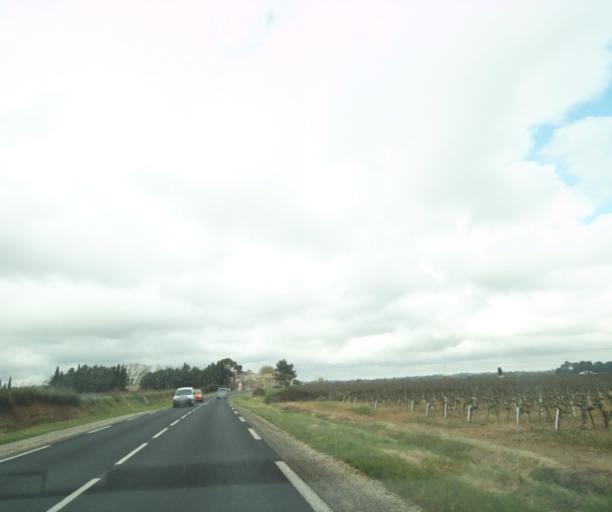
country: FR
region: Languedoc-Roussillon
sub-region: Departement de l'Herault
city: Pignan
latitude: 43.5926
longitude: 3.7741
